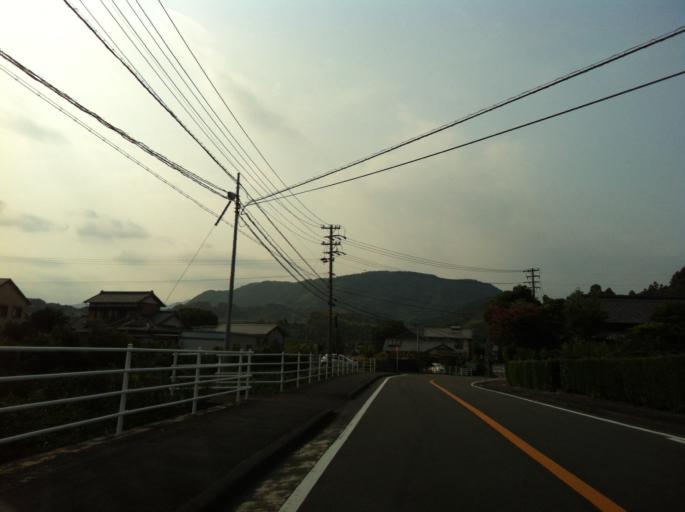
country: JP
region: Shizuoka
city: Fujieda
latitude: 34.9121
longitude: 138.2706
